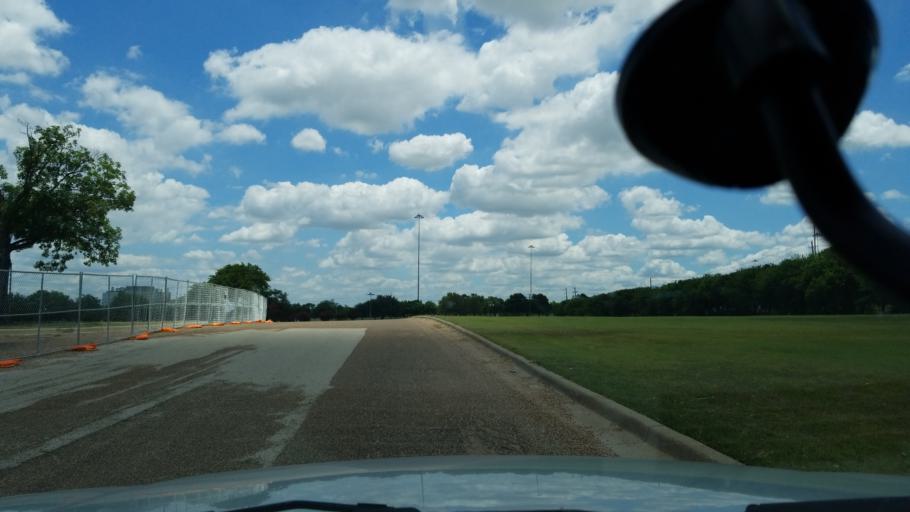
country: US
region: Texas
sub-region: Dallas County
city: Duncanville
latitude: 32.6571
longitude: -96.8800
